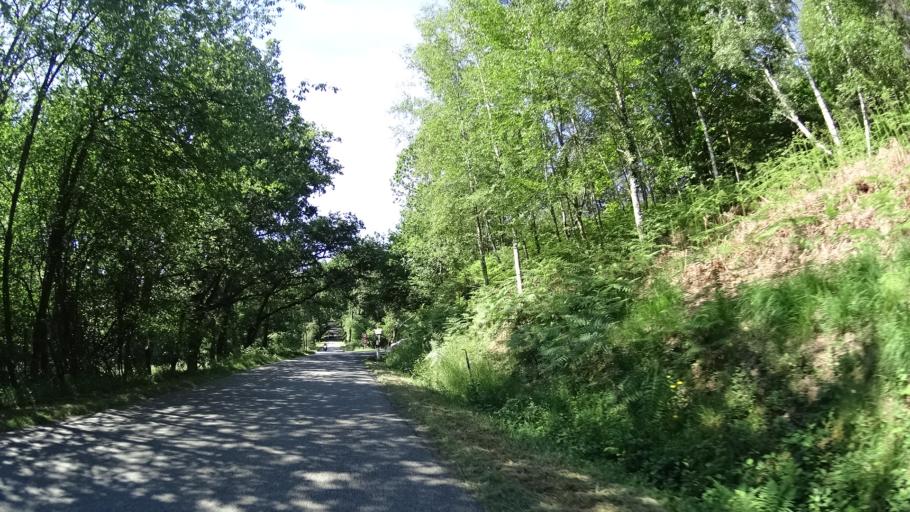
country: FR
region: Brittany
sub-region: Departement d'Ille-et-Vilaine
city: Langon
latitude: 47.7693
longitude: -1.8471
